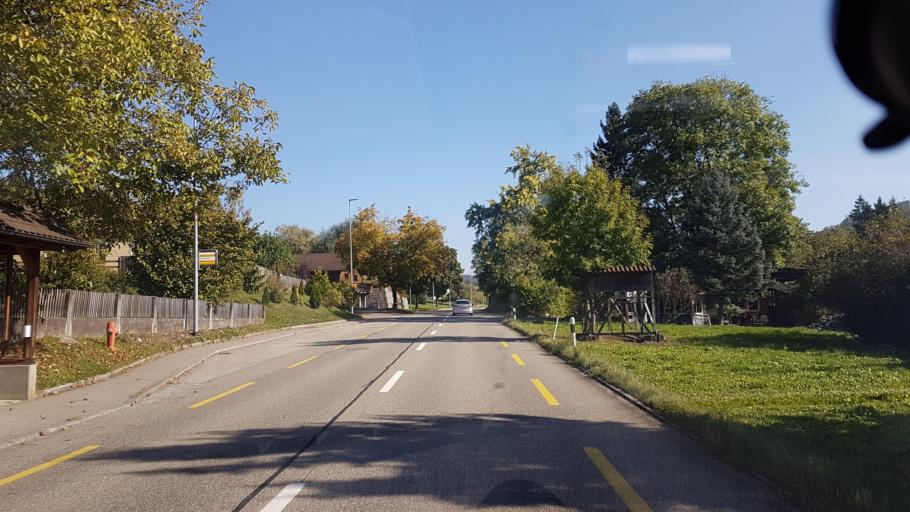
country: CH
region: Aargau
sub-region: Bezirk Laufenburg
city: Sulz
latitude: 47.4935
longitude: 8.0895
